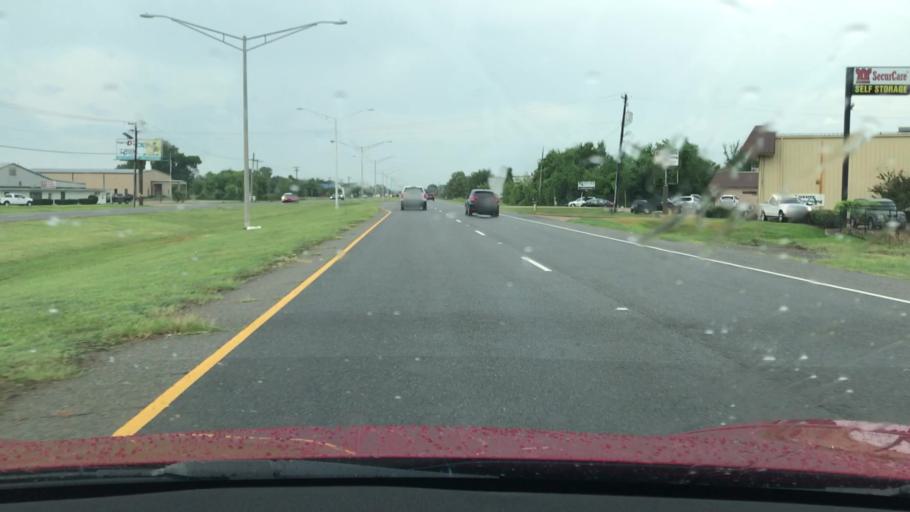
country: US
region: Louisiana
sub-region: Bossier Parish
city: Bossier City
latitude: 32.4042
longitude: -93.6959
